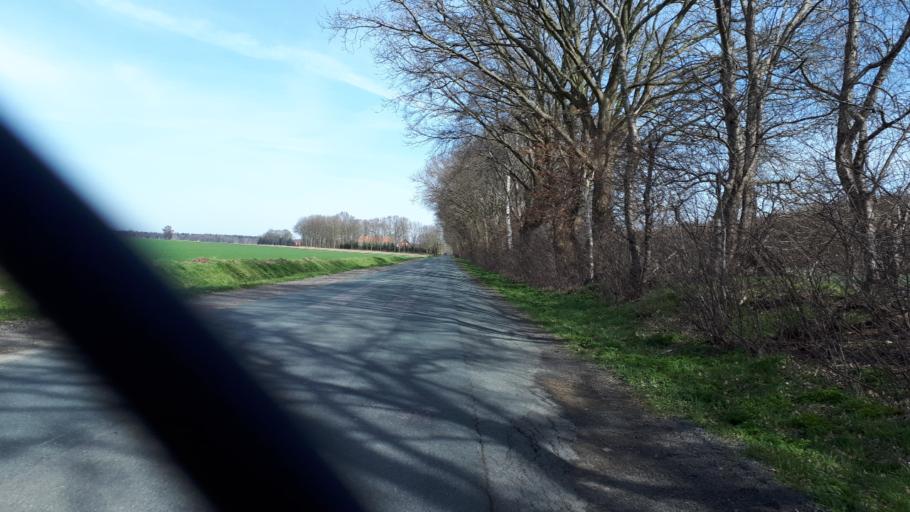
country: DE
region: Lower Saxony
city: Cloppenburg
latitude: 52.8713
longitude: 7.9979
